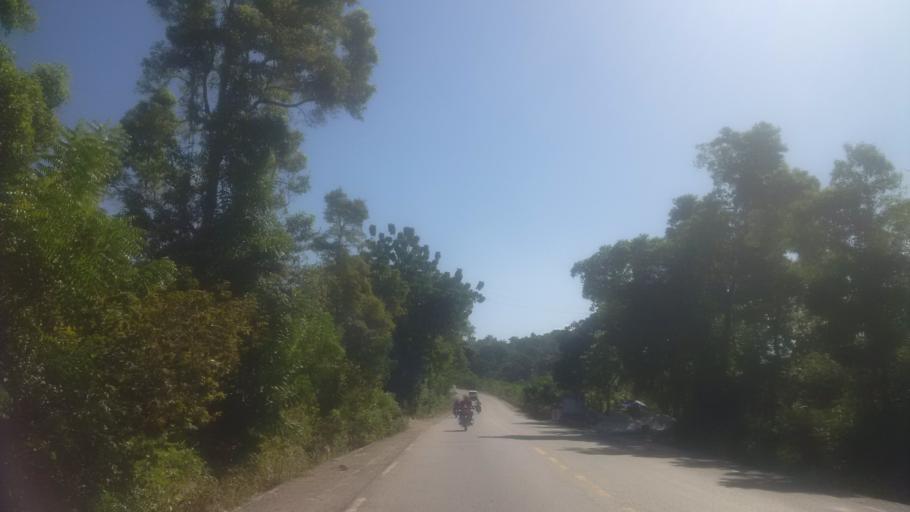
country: HT
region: Ouest
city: Tigwav
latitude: 18.4330
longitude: -72.8230
